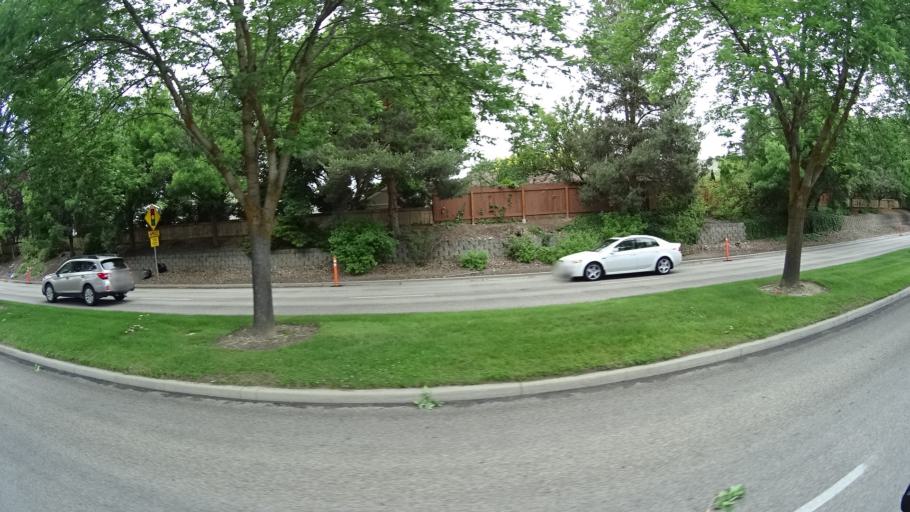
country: US
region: Idaho
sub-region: Ada County
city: Boise
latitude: 43.5825
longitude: -116.1707
